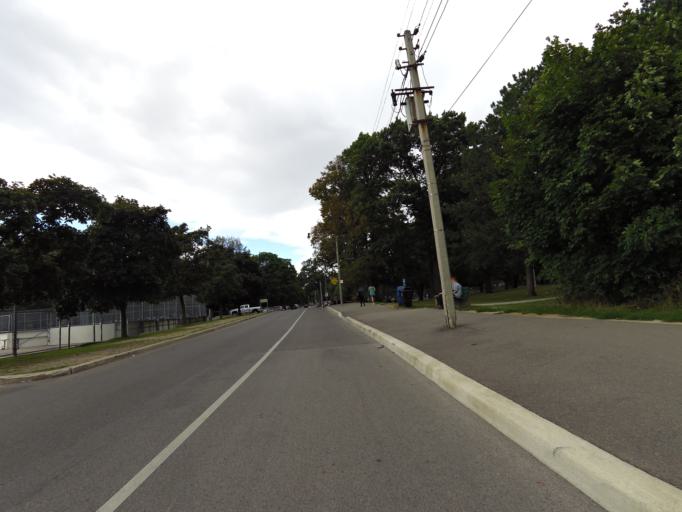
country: CA
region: Ontario
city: Toronto
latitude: 43.6496
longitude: -79.4649
